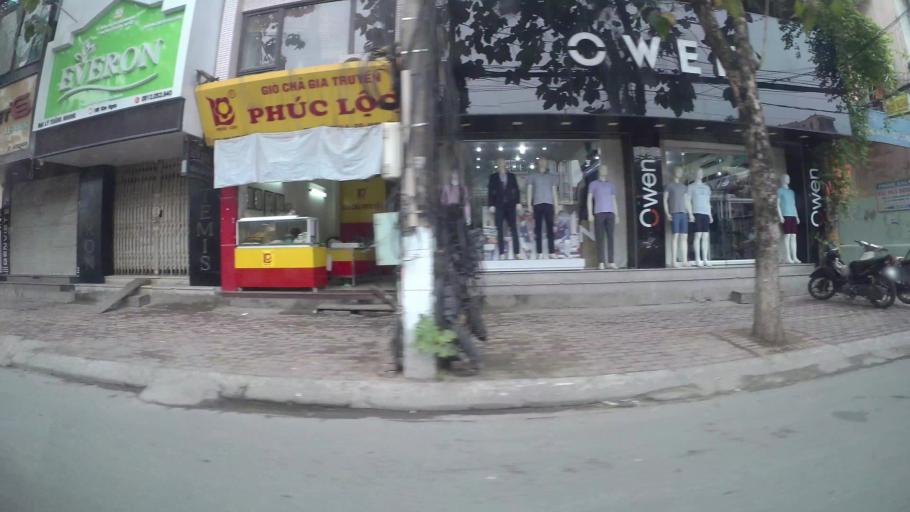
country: VN
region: Ha Noi
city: Hai BaTrung
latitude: 21.0033
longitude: 105.8612
